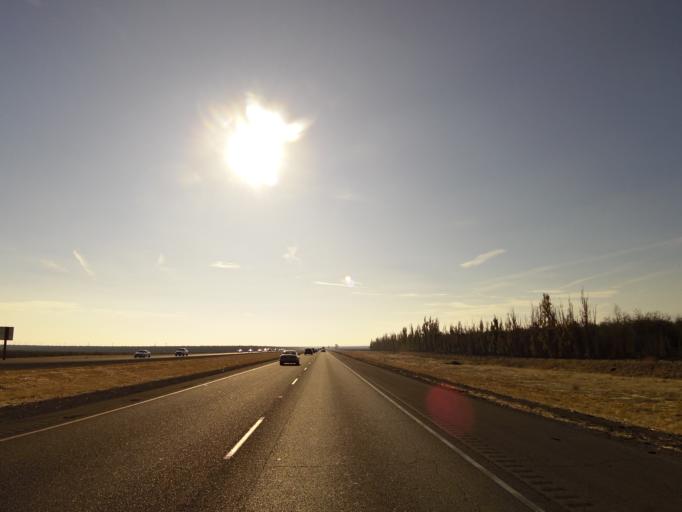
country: US
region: California
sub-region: Merced County
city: South Dos Palos
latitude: 36.8038
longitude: -120.7423
